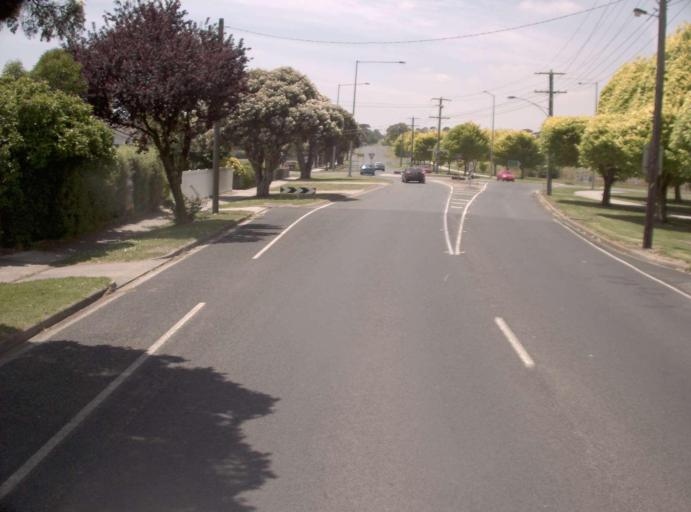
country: AU
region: Victoria
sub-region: Latrobe
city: Traralgon
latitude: -38.2013
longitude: 146.5433
